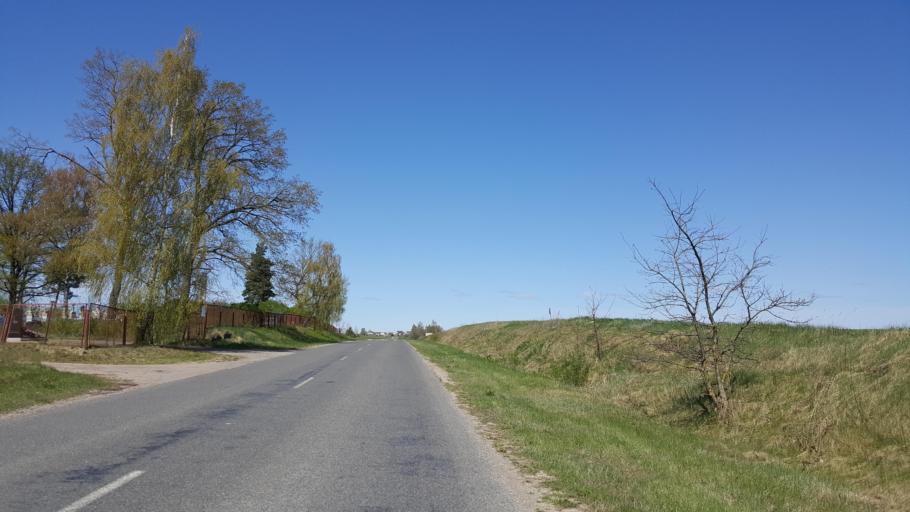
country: BY
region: Brest
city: Charnawchytsy
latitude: 52.3311
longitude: 23.6065
